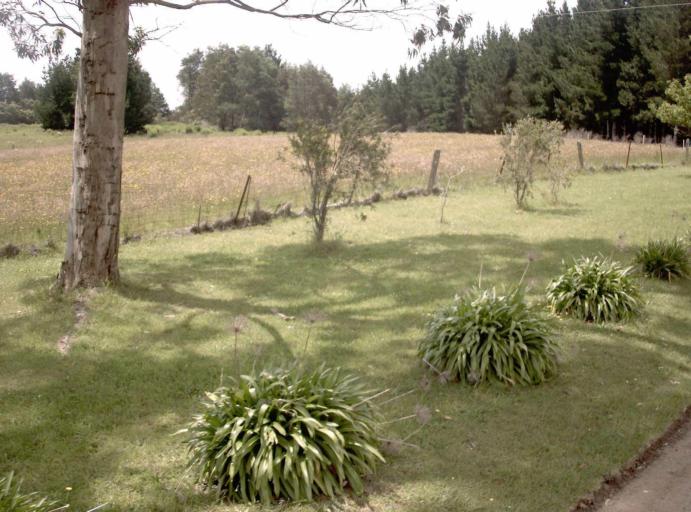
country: AU
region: Victoria
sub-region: Latrobe
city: Traralgon
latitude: -38.4155
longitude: 146.6166
